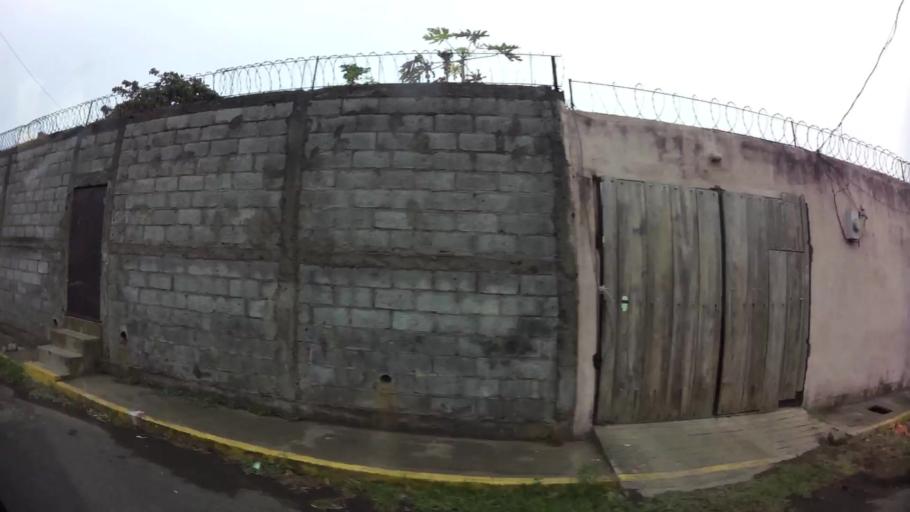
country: NI
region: Leon
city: Leon
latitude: 12.4488
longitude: -86.8728
